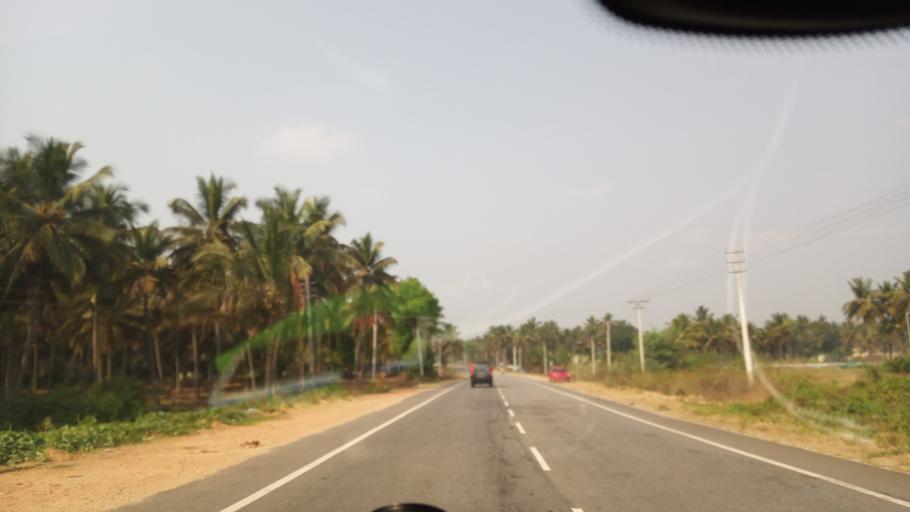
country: IN
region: Karnataka
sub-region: Mandya
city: Nagamangala
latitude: 12.7406
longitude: 76.7247
